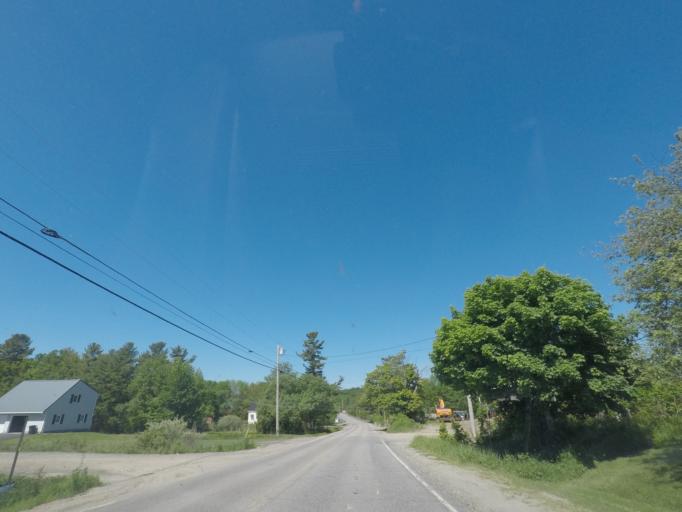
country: US
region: Maine
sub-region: Kennebec County
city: Gardiner
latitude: 44.2309
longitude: -69.8080
